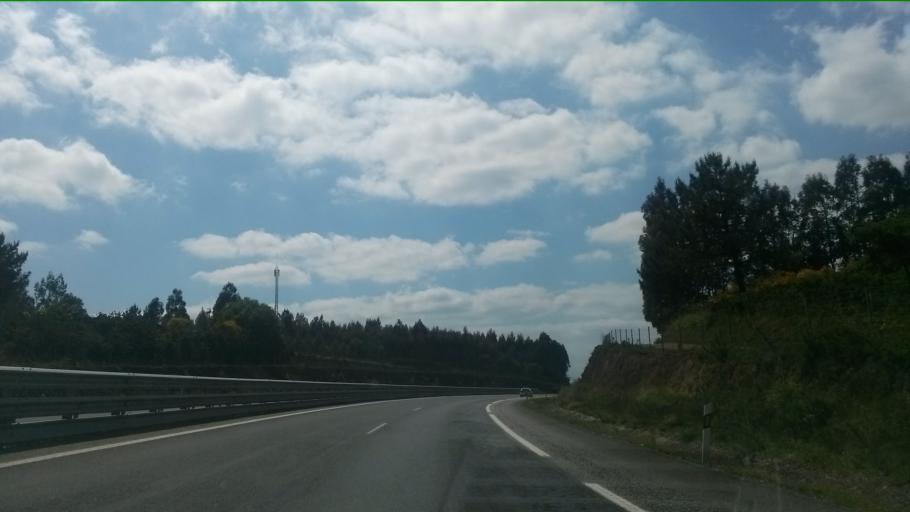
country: ES
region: Galicia
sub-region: Provincia da Coruna
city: Oroso
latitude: 42.9103
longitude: -8.4495
